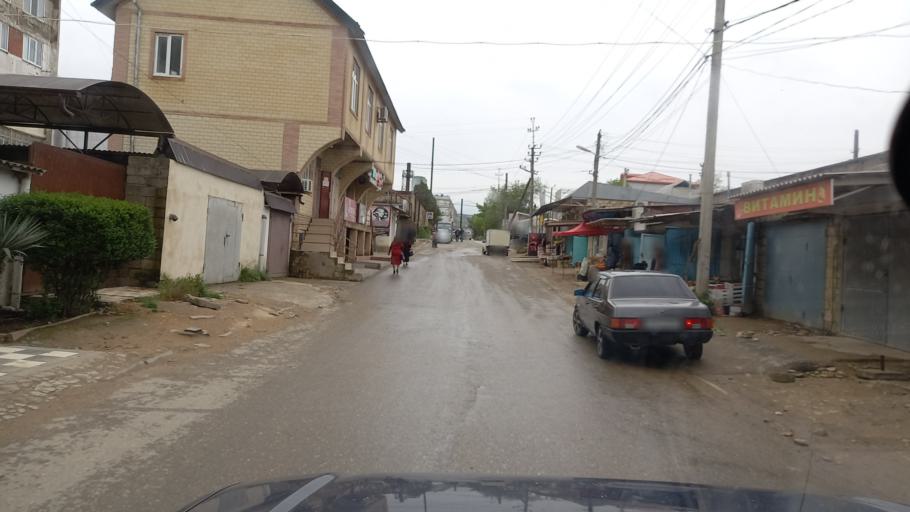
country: RU
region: Dagestan
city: Derbent
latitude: 42.0865
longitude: 48.2912
